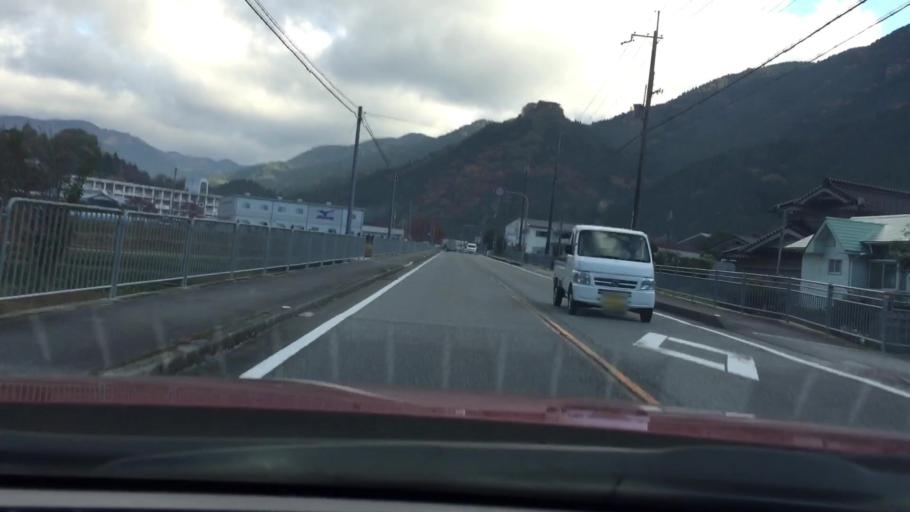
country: JP
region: Hyogo
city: Yamazakicho-nakabirose
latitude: 35.1510
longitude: 134.5417
